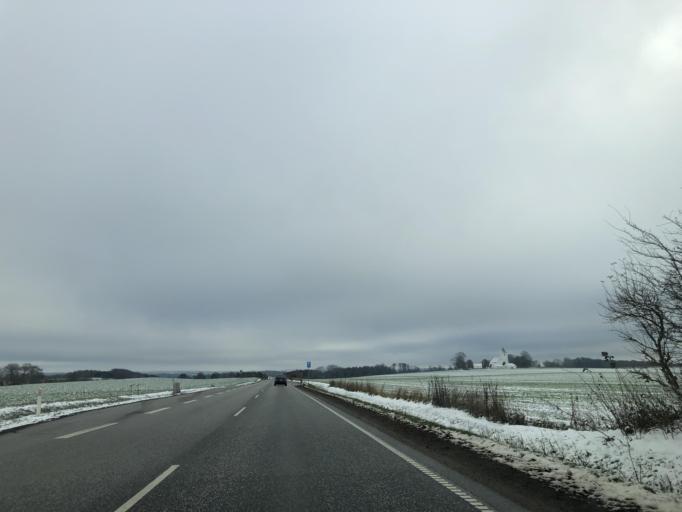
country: DK
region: Central Jutland
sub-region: Hedensted Kommune
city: Hedensted
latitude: 55.8953
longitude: 9.7267
